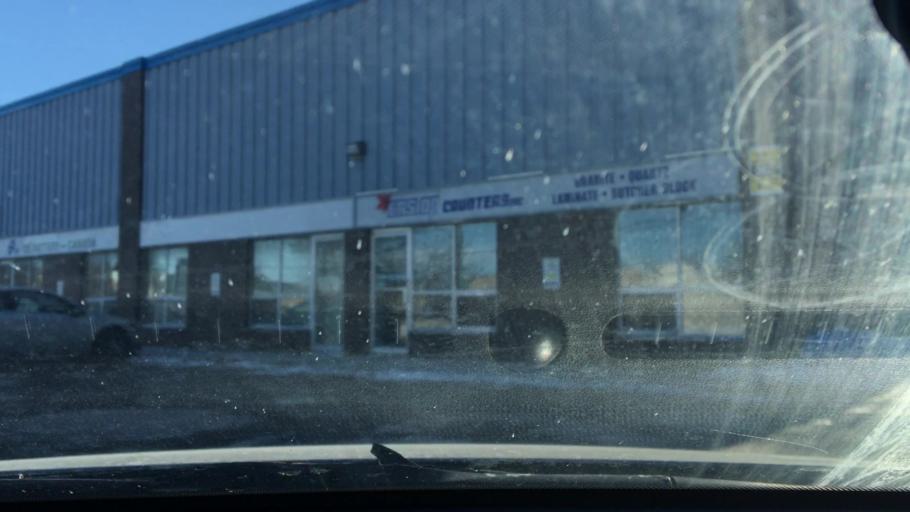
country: CA
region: Ontario
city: Ottawa
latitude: 45.3964
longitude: -75.6066
